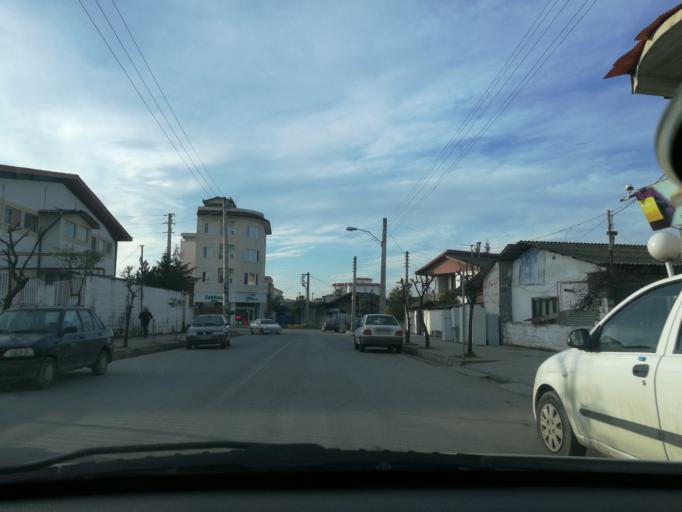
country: IR
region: Mazandaran
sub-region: Nowshahr
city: Nowshahr
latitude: 36.6405
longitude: 51.5038
